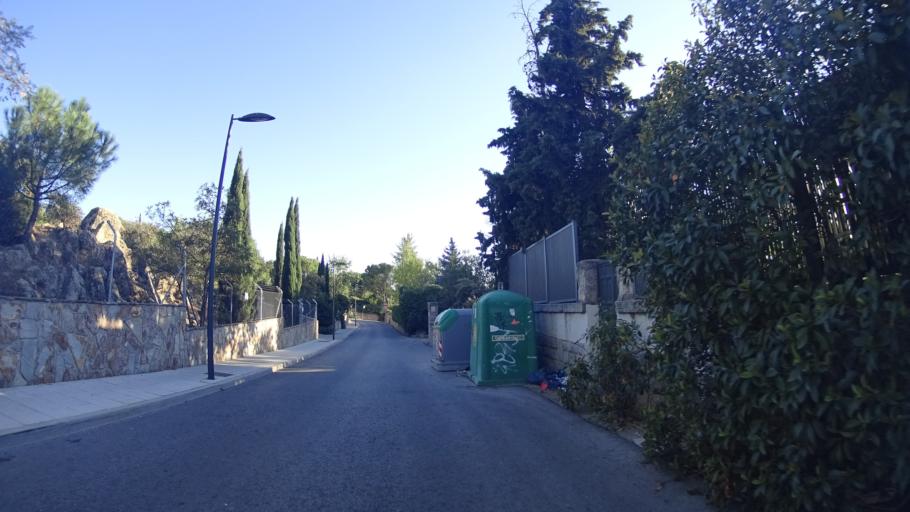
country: ES
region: Madrid
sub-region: Provincia de Madrid
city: Torrelodones
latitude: 40.5753
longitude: -3.9428
